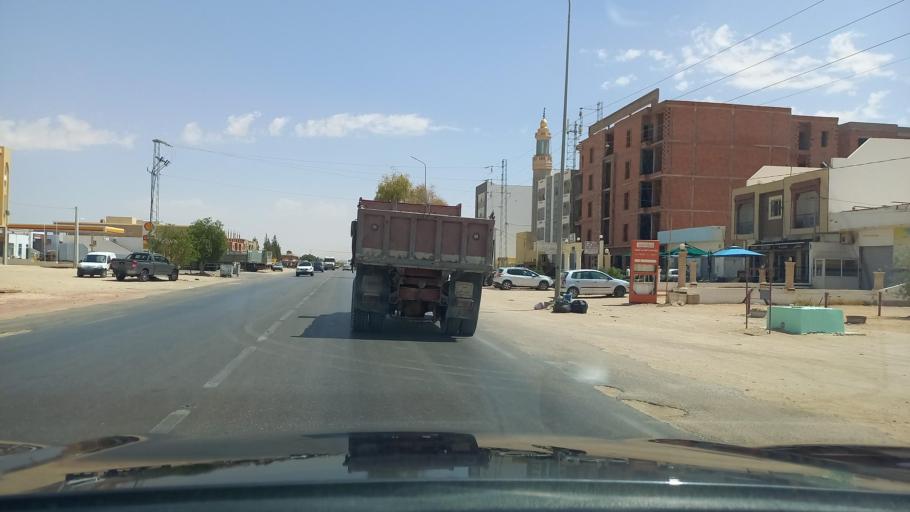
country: TN
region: Madanin
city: Medenine
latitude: 33.3656
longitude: 10.4585
